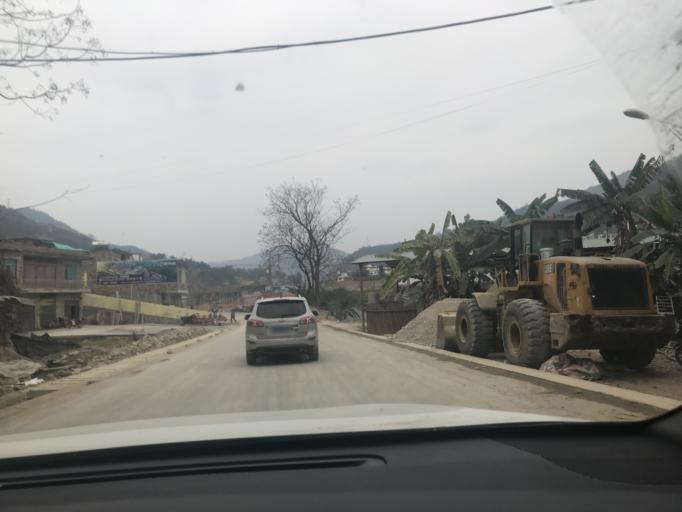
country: CN
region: Guangxi Zhuangzu Zizhiqu
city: Xinzhou
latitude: 25.0122
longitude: 105.8575
